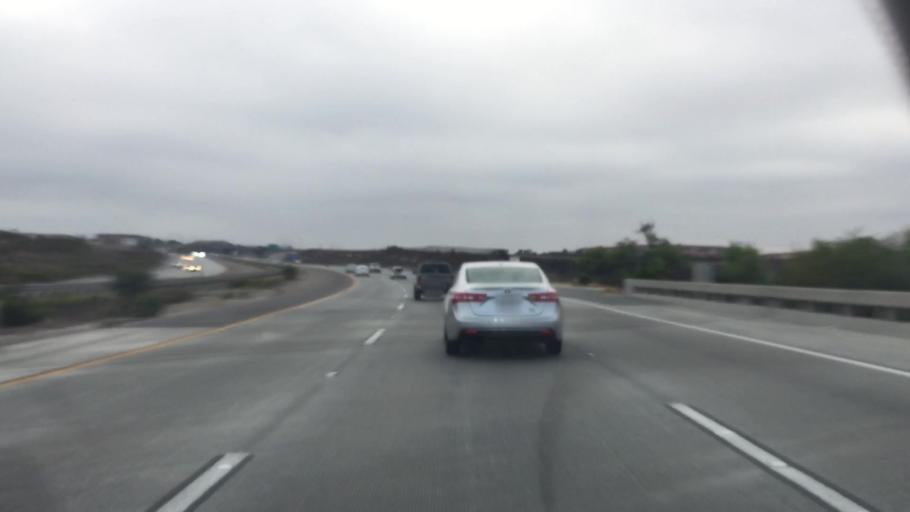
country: MX
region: Baja California
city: Tijuana
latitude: 32.5665
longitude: -117.0039
